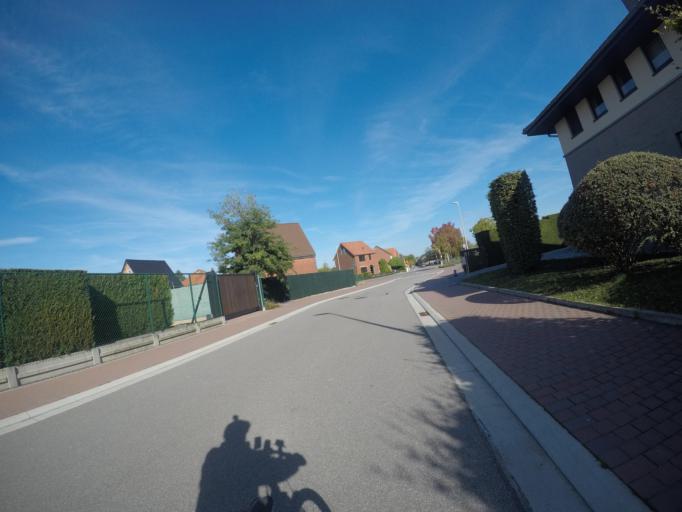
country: BE
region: Flanders
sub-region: Provincie Limburg
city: Diepenbeek
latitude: 50.9032
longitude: 5.4208
